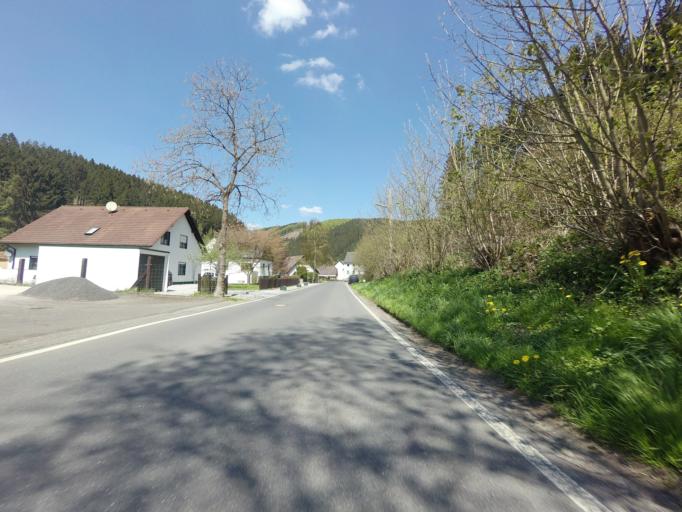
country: DE
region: North Rhine-Westphalia
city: Hemer
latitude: 51.3471
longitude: 7.7927
